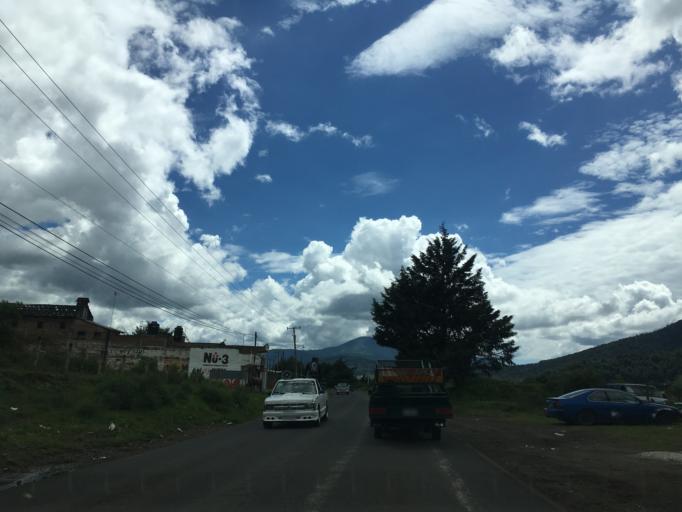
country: MX
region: Michoacan
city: Cheran
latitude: 19.6733
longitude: -101.9512
